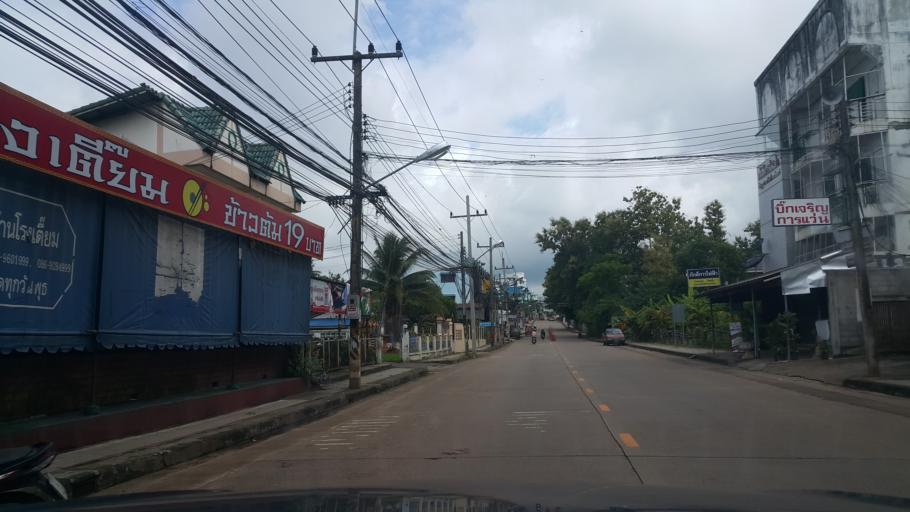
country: TH
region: Uttaradit
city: Uttaradit
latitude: 17.6147
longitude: 100.0892
